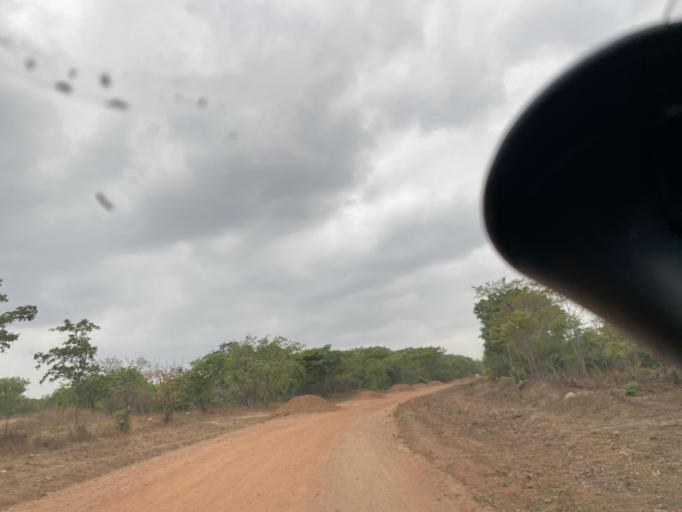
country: ZM
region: Lusaka
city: Chongwe
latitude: -15.2259
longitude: 28.7357
